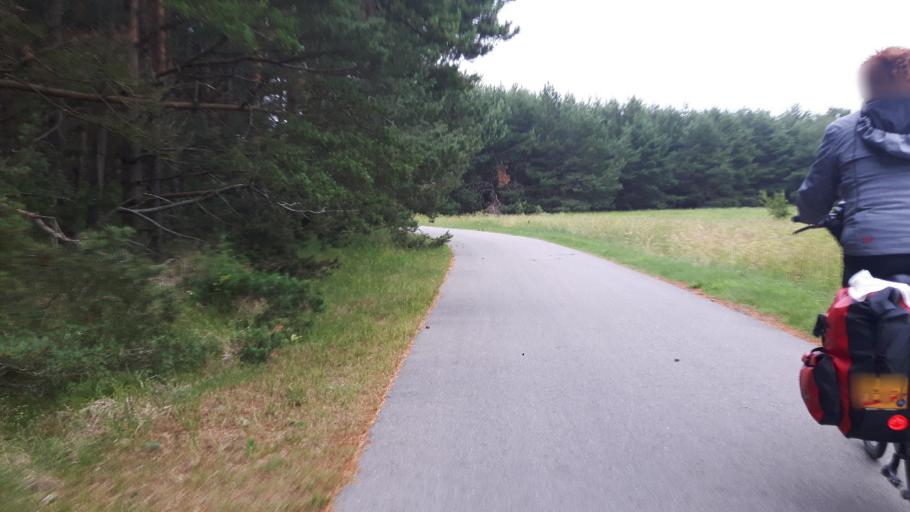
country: LT
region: Klaipedos apskritis
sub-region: Palanga
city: Sventoji
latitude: 55.9916
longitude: 21.0749
